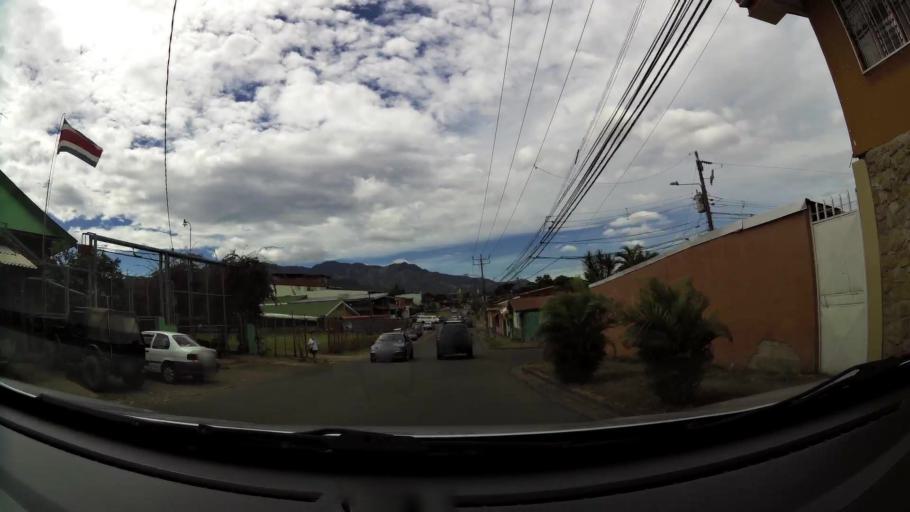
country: CR
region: San Jose
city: San Miguel
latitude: 9.8920
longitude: -84.0597
